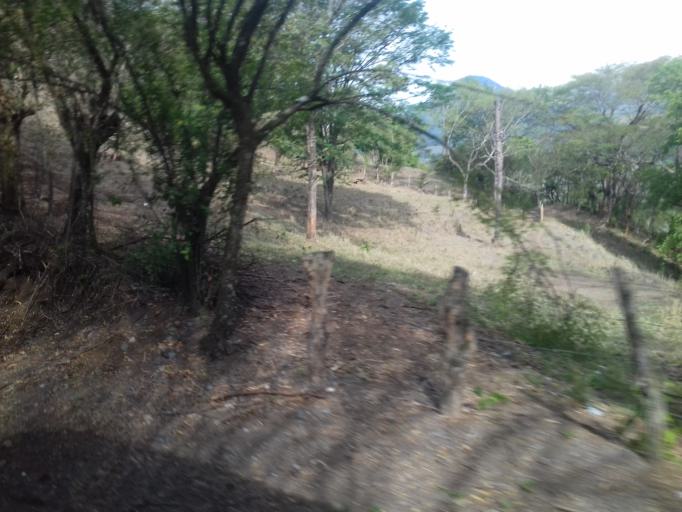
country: CO
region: Antioquia
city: Titiribi
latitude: 5.9805
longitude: -75.8270
